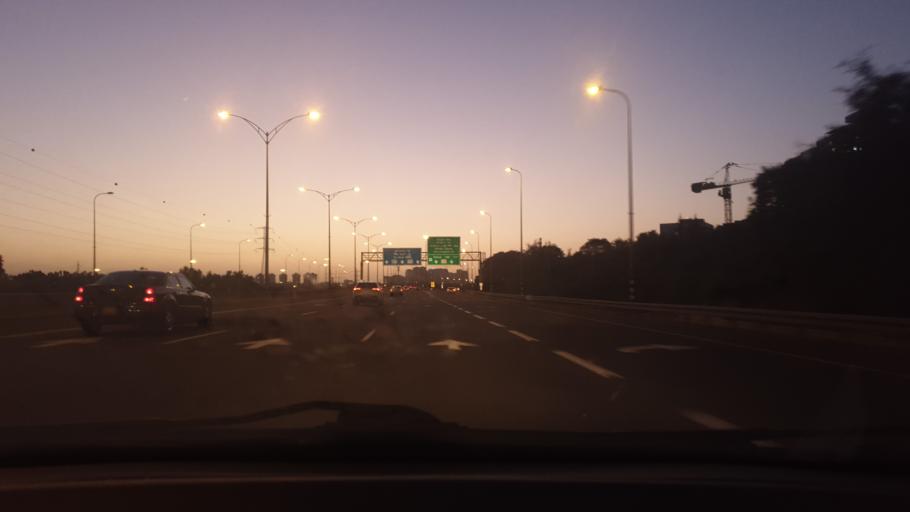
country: IL
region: Central District
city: Nehalim
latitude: 32.0671
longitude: 34.9108
